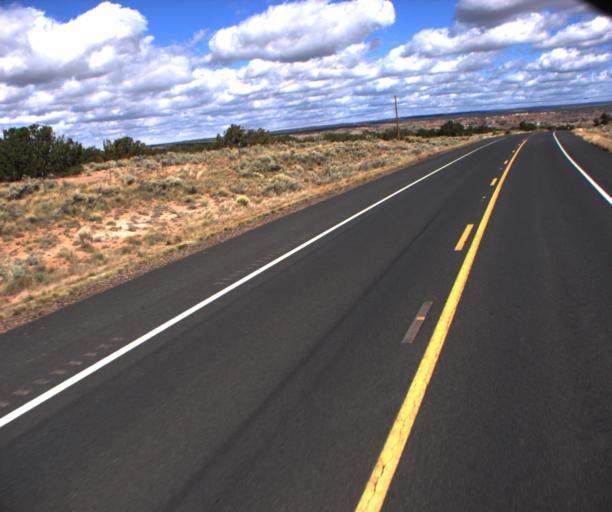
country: US
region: Arizona
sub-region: Apache County
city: Houck
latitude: 35.1813
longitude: -109.3376
